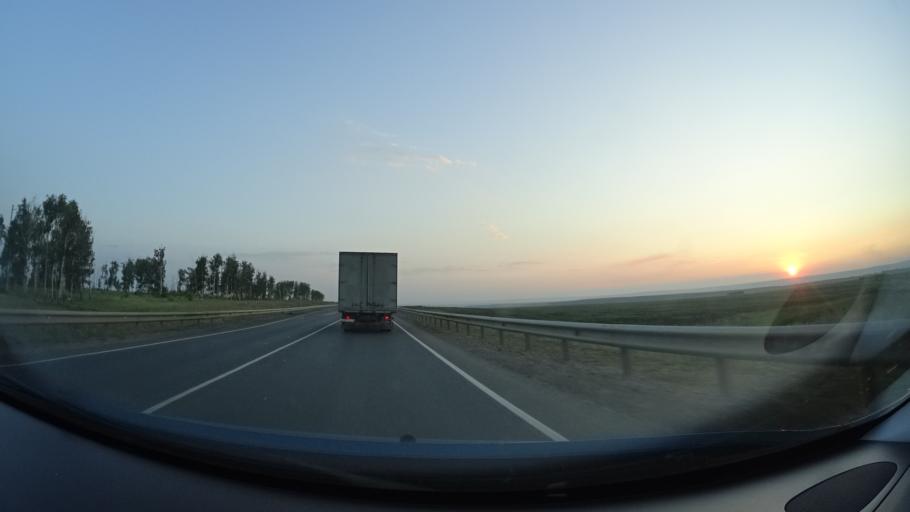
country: RU
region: Samara
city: Sukhodol
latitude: 53.8221
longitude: 51.0519
